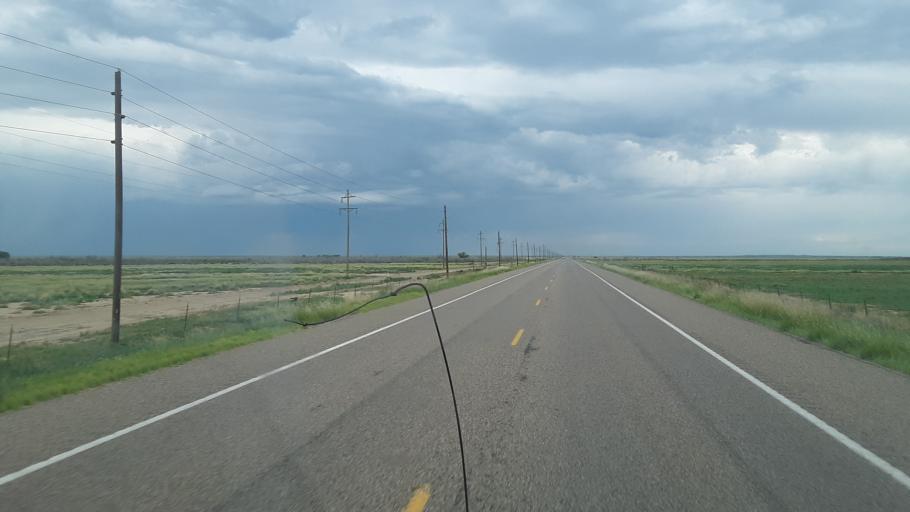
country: US
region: Colorado
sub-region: Crowley County
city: Ordway
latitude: 38.1870
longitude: -103.7482
